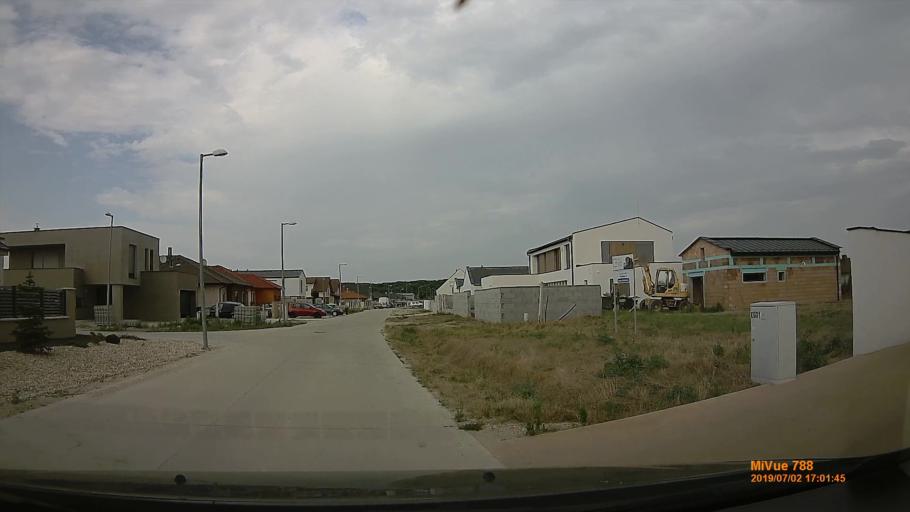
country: HU
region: Gyor-Moson-Sopron
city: Halaszi
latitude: 47.8897
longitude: 17.2948
